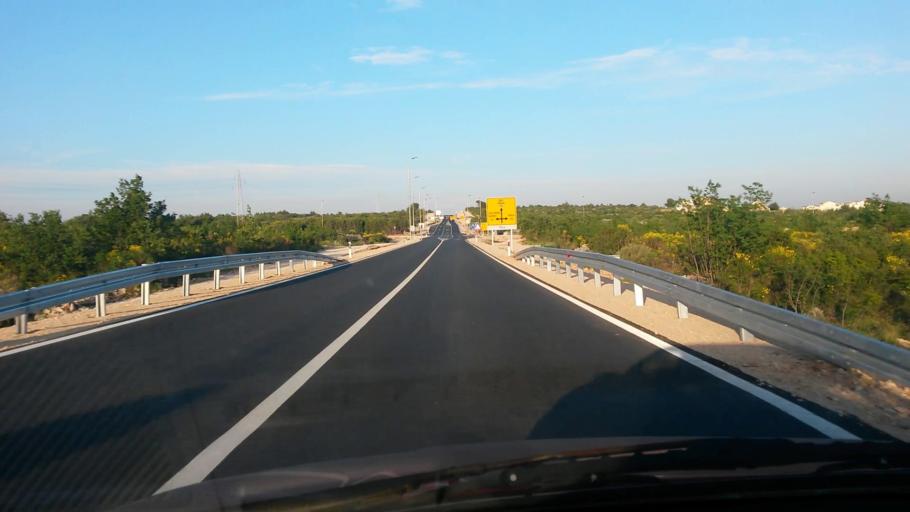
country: HR
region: Sibensko-Kniniska
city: Vodice
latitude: 43.7755
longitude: 15.7703
